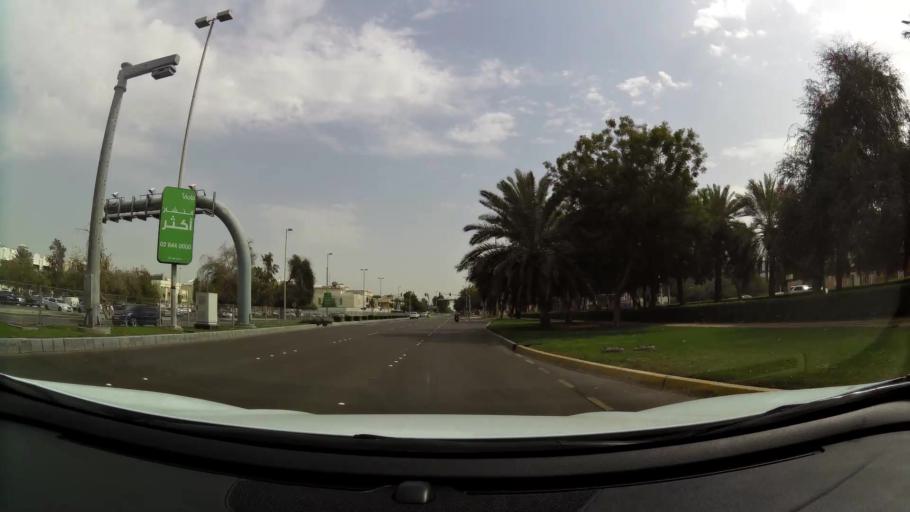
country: AE
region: Abu Dhabi
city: Abu Dhabi
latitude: 24.4668
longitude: 54.3650
